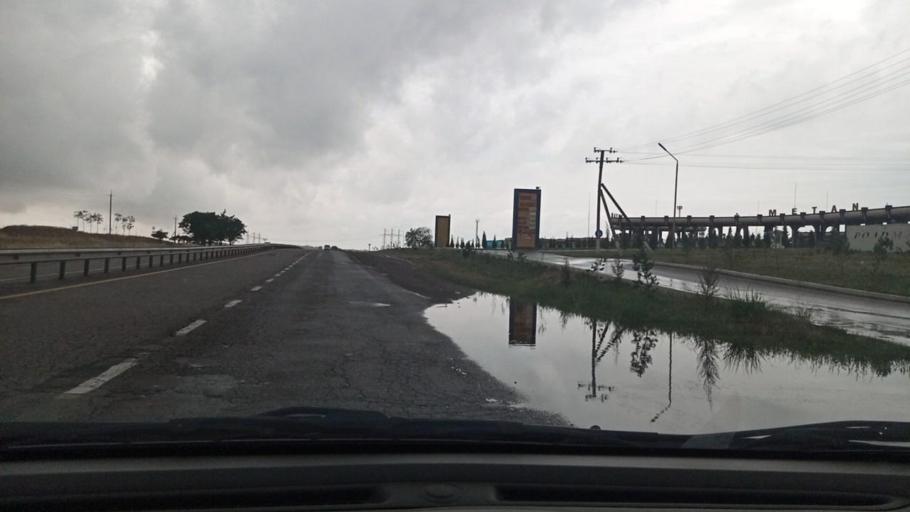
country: UZ
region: Toshkent
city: Ohangaron
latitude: 40.9400
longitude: 69.5832
